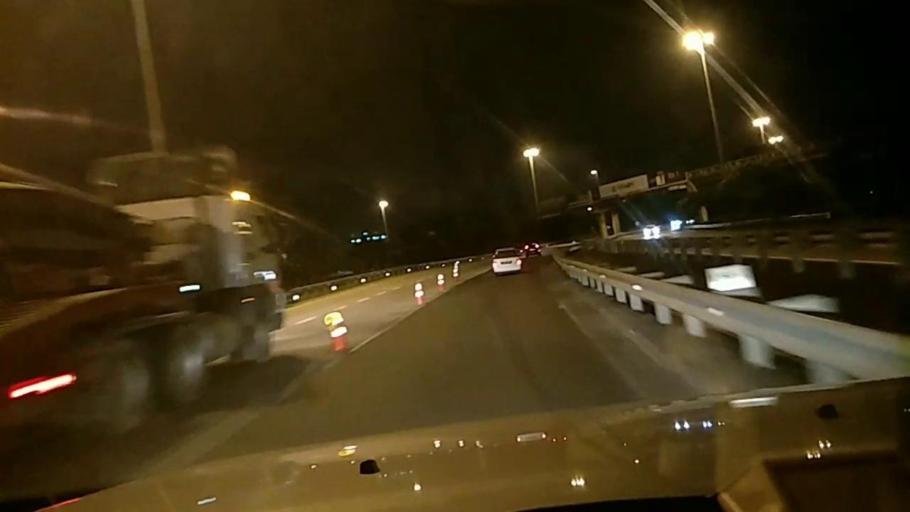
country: MY
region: Penang
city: Perai
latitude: 5.3653
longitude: 100.3993
